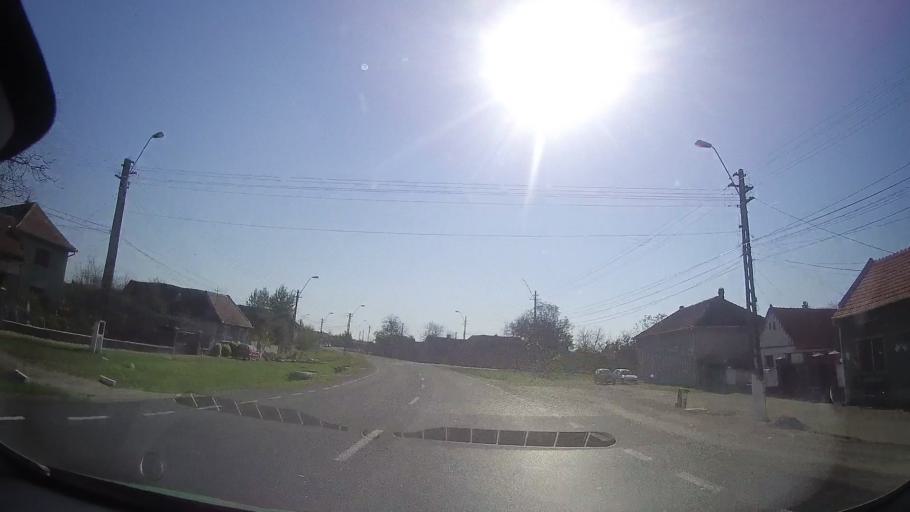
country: RO
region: Timis
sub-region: Comuna Belint
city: Belint
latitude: 45.7588
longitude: 21.7304
